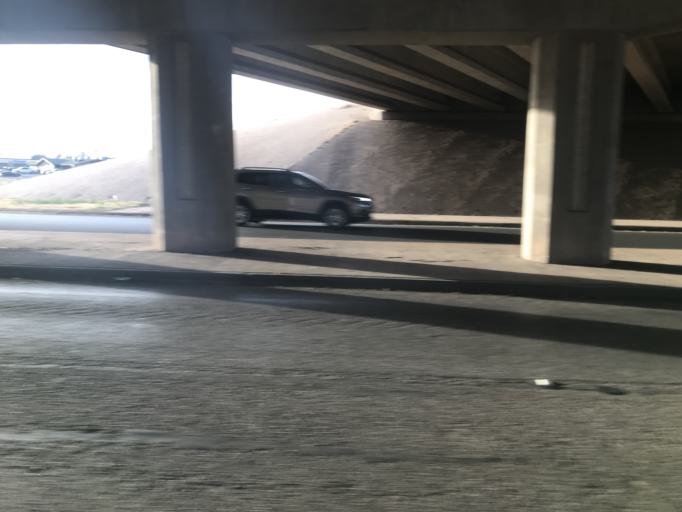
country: US
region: Texas
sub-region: Taylor County
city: Abilene
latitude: 32.4269
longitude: -99.7859
